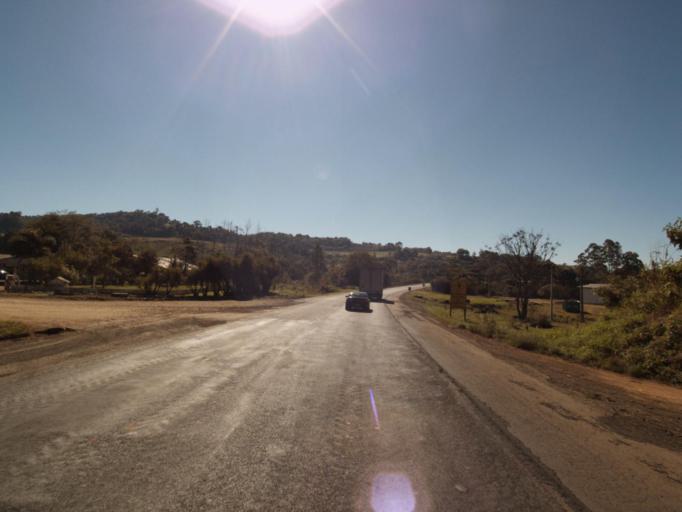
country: BR
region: Rio Grande do Sul
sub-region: Frederico Westphalen
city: Frederico Westphalen
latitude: -26.8967
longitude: -53.1906
